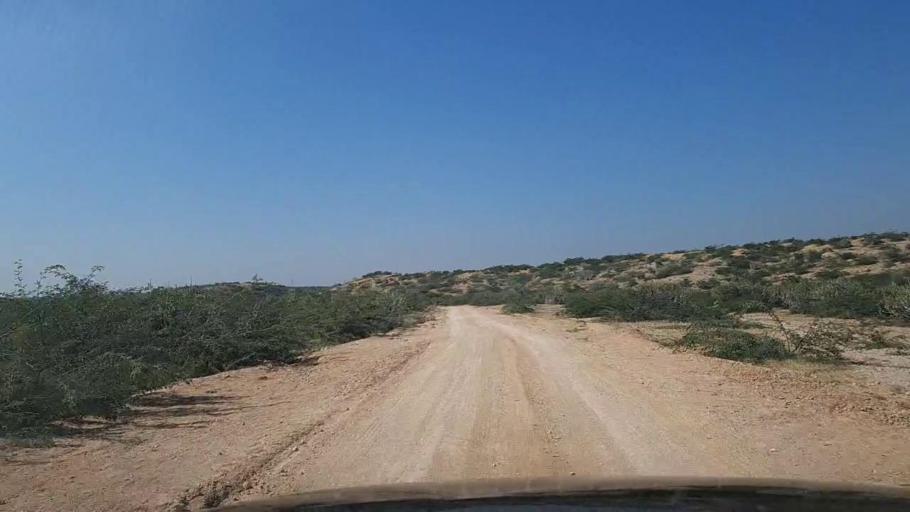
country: PK
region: Sindh
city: Thatta
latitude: 24.6216
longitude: 67.8443
